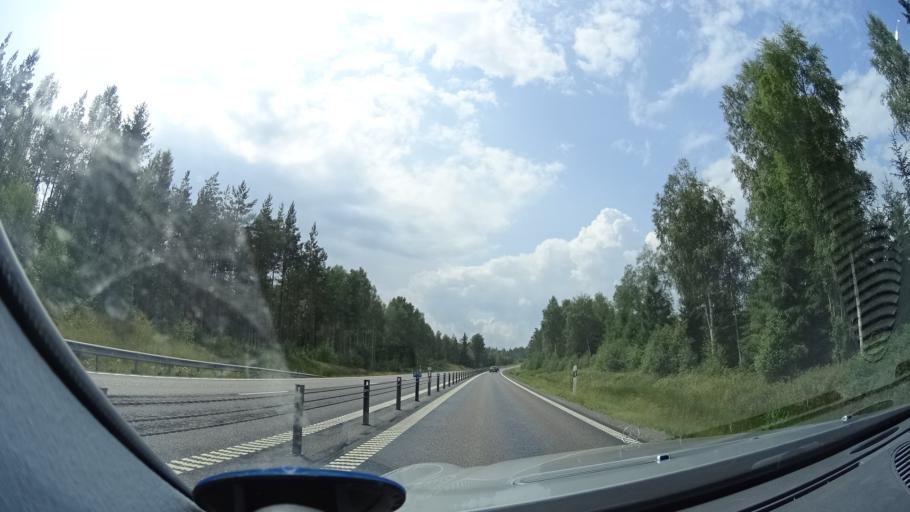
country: SE
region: Kalmar
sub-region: Nybro Kommun
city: Nybro
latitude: 56.7262
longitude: 15.8242
